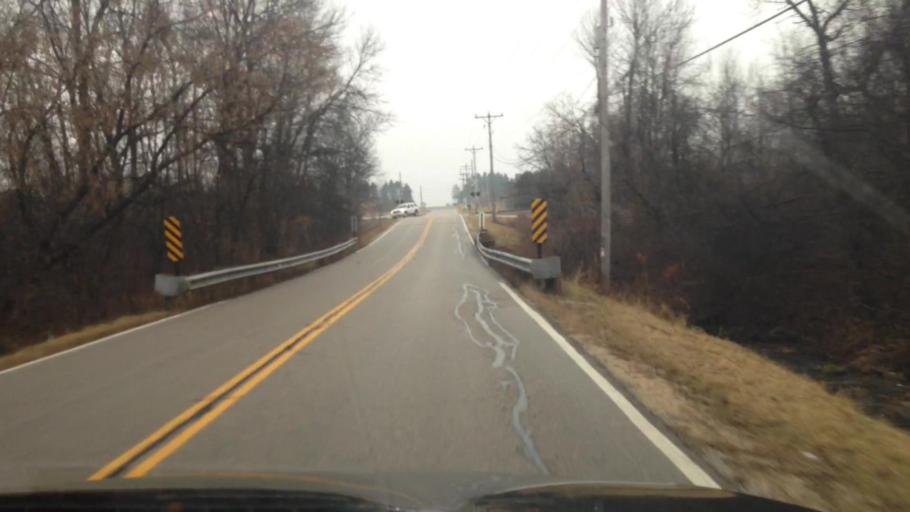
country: US
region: Wisconsin
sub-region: Washington County
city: Germantown
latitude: 43.2393
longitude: -88.1430
